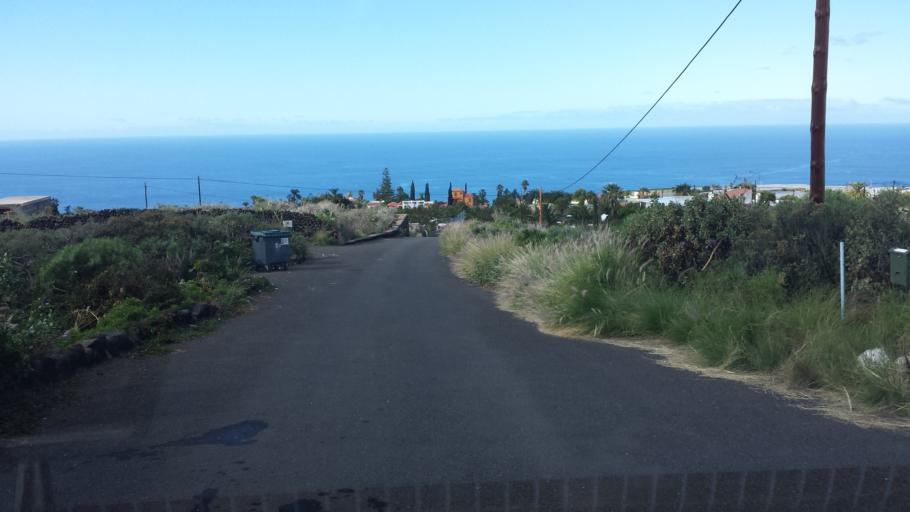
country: ES
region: Canary Islands
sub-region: Provincia de Santa Cruz de Tenerife
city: Tazacorte
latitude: 28.6079
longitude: -17.9040
